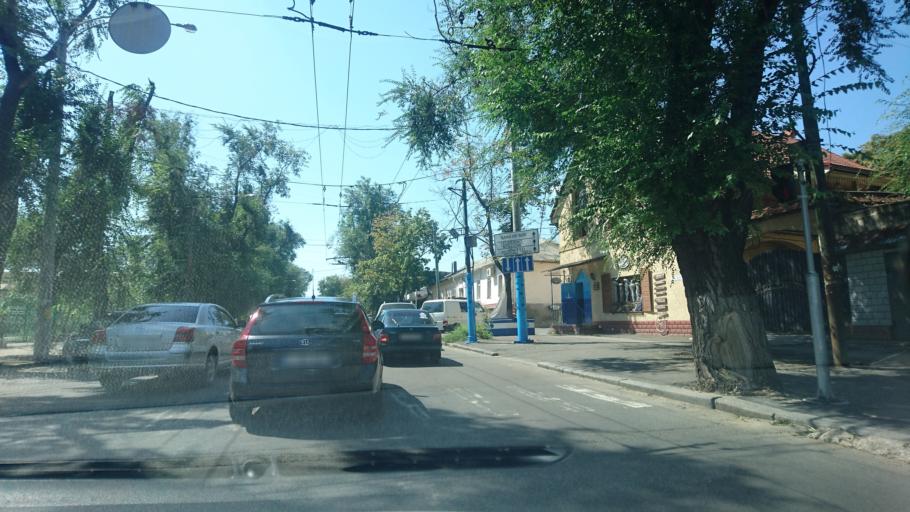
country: MD
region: Chisinau
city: Chisinau
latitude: 47.0137
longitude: 28.8280
